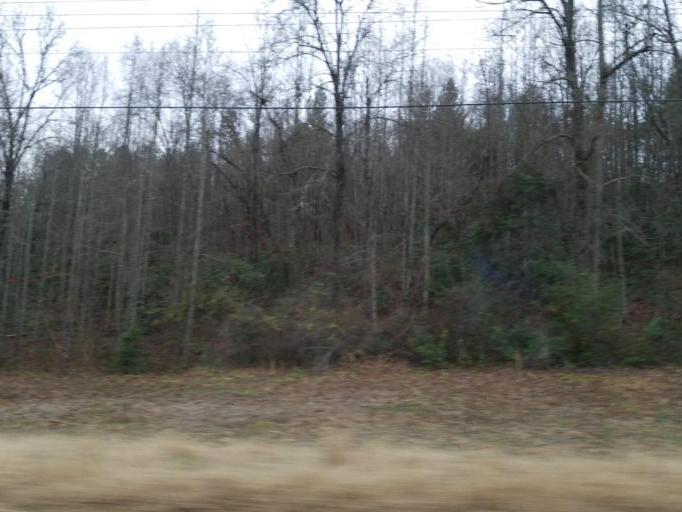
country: US
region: Georgia
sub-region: Dawson County
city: Dawsonville
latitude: 34.5158
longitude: -84.2394
